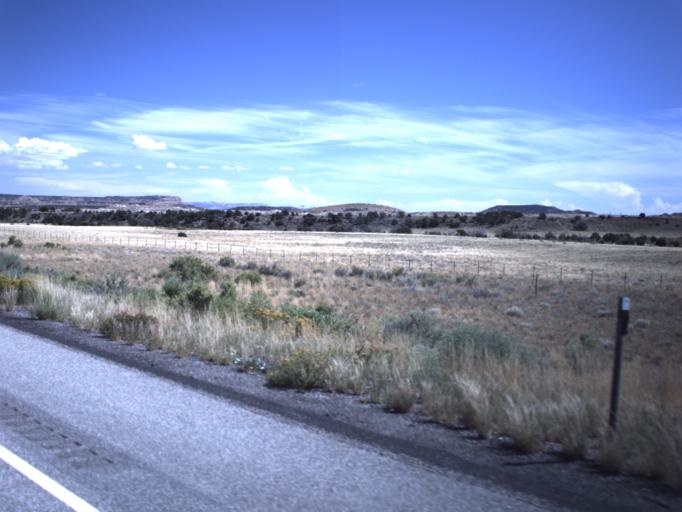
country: US
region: Utah
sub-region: Emery County
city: Ferron
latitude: 38.7757
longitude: -111.3220
